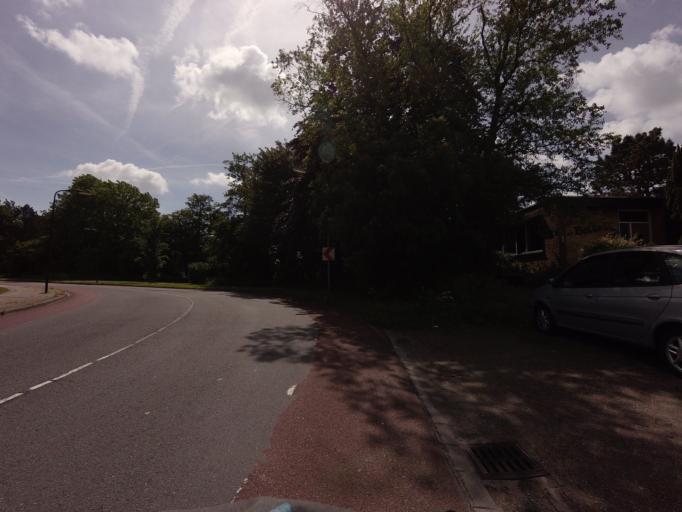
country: NL
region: North Holland
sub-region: Gemeente Hoorn
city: Hoorn
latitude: 52.6451
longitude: 5.0413
